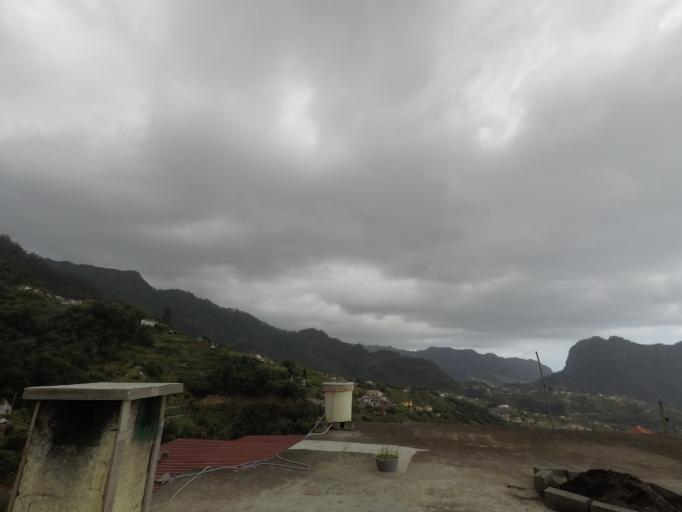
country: PT
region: Madeira
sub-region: Santa Cruz
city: Santa Cruz
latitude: 32.7522
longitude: -16.8262
